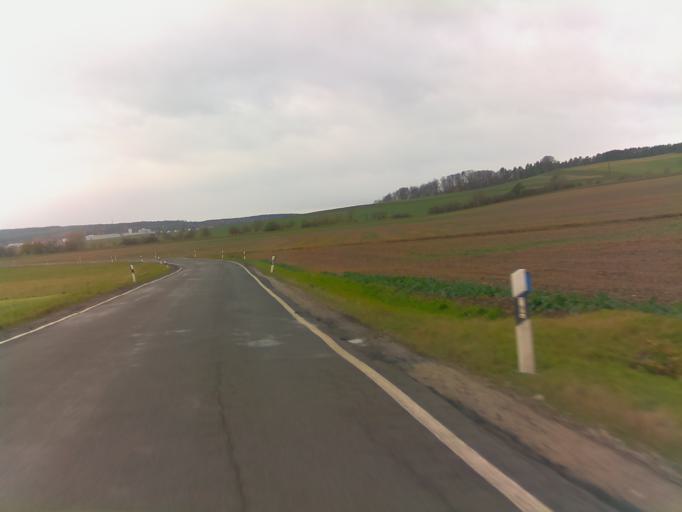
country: DE
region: Thuringia
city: Blankenhain
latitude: 50.8537
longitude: 11.3902
